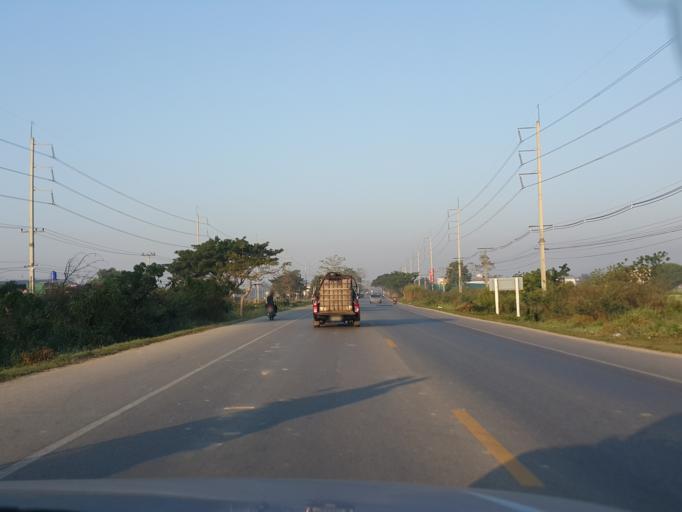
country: TH
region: Chiang Mai
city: Saraphi
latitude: 18.7201
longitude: 98.9988
